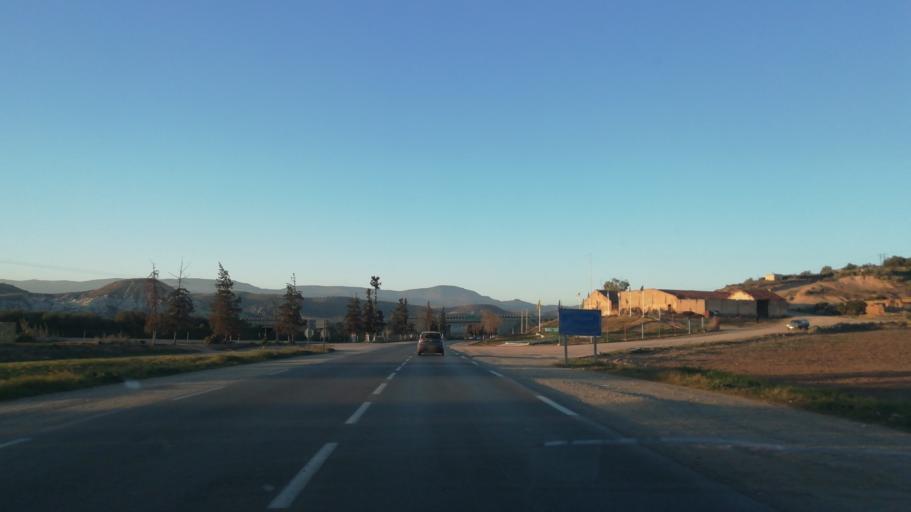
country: DZ
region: Tlemcen
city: Nedroma
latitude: 34.8983
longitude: -1.6385
